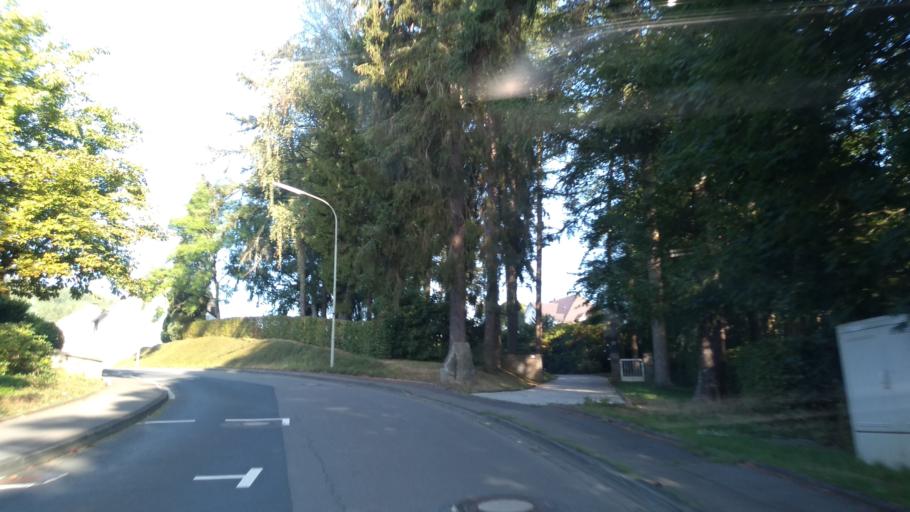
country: DE
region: North Rhine-Westphalia
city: Wiehl
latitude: 50.9618
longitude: 7.4970
